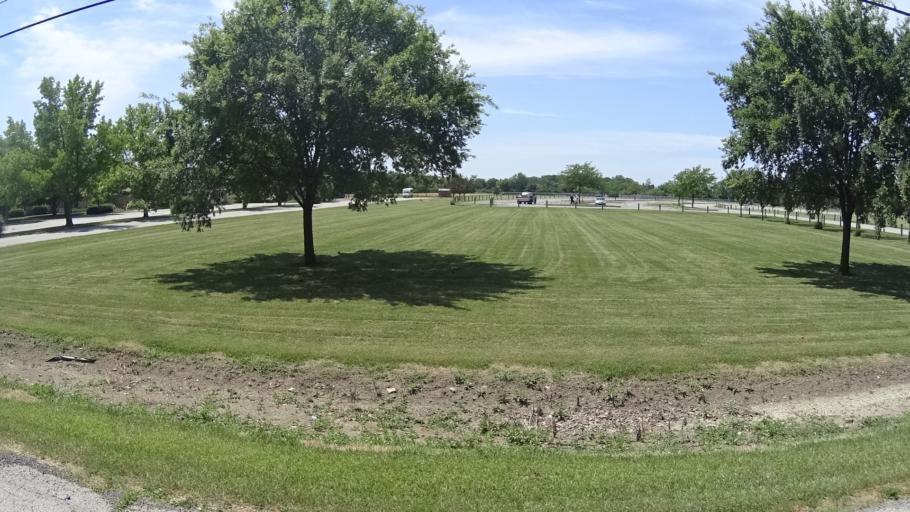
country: US
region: Ohio
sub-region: Erie County
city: Sandusky
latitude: 41.4392
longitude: -82.7726
